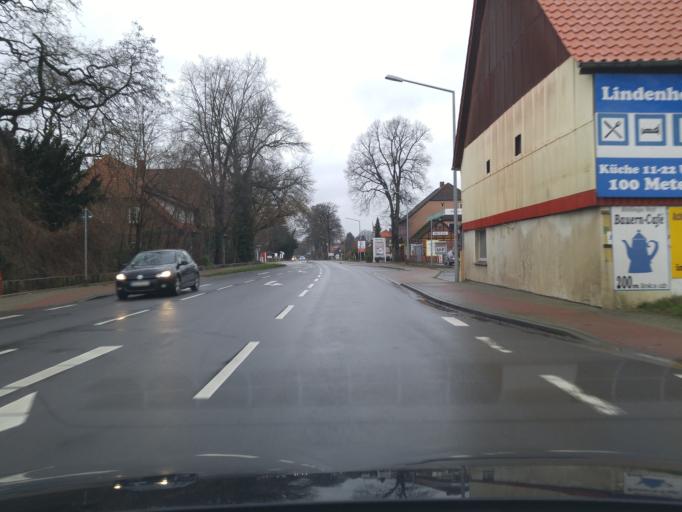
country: DE
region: Lower Saxony
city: Sprakensehl
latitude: 52.7654
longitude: 10.4941
